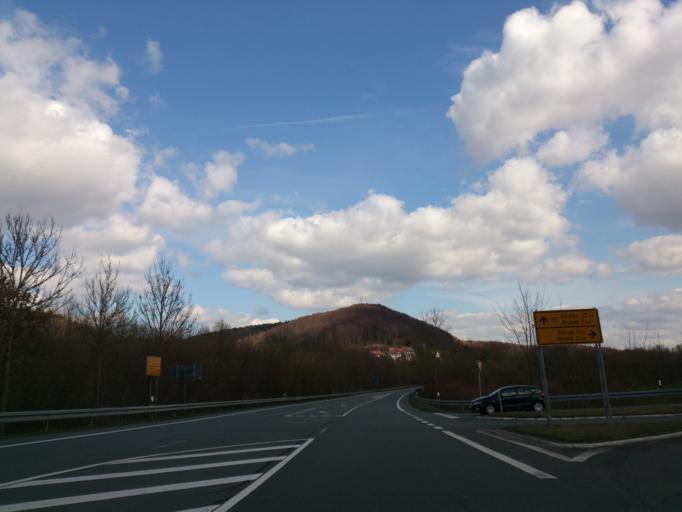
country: DE
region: North Rhine-Westphalia
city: Brakel
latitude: 51.7114
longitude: 9.1120
